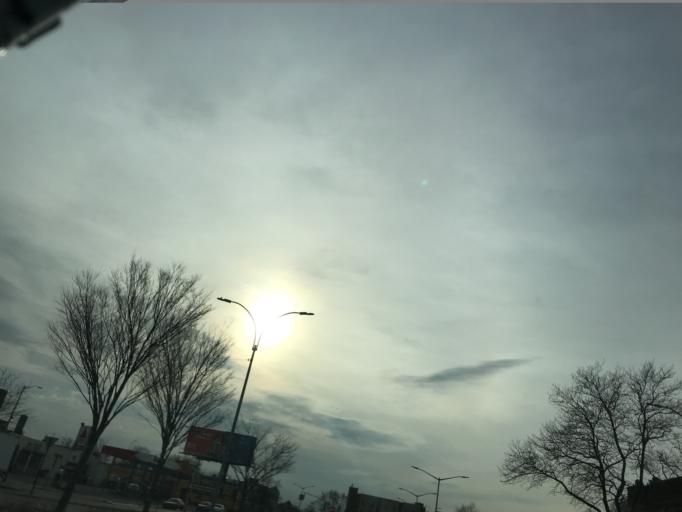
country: US
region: New York
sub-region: Kings County
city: East New York
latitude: 40.6583
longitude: -73.8915
